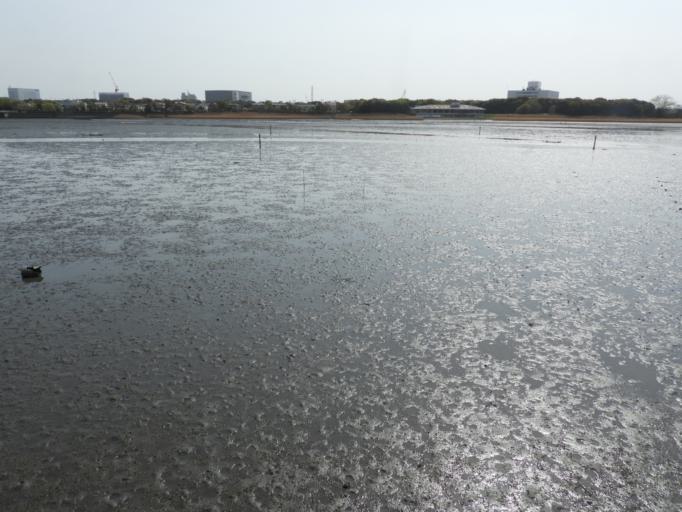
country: JP
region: Chiba
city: Funabashi
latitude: 35.6785
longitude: 140.0089
